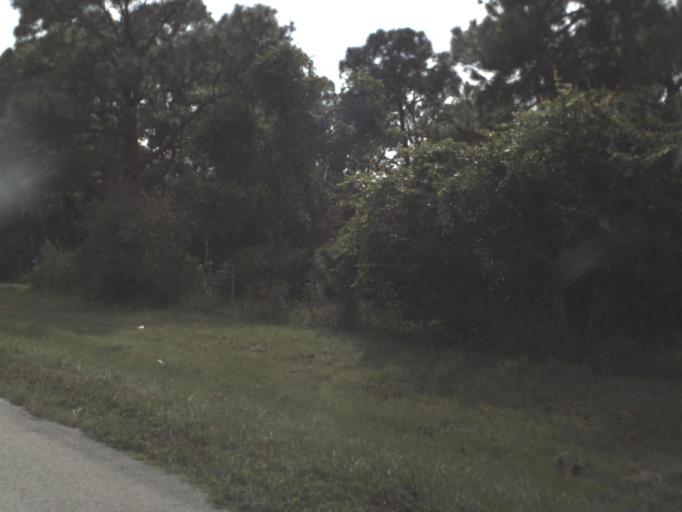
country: US
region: Florida
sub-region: Okeechobee County
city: Cypress Quarters
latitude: 27.2845
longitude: -80.8287
